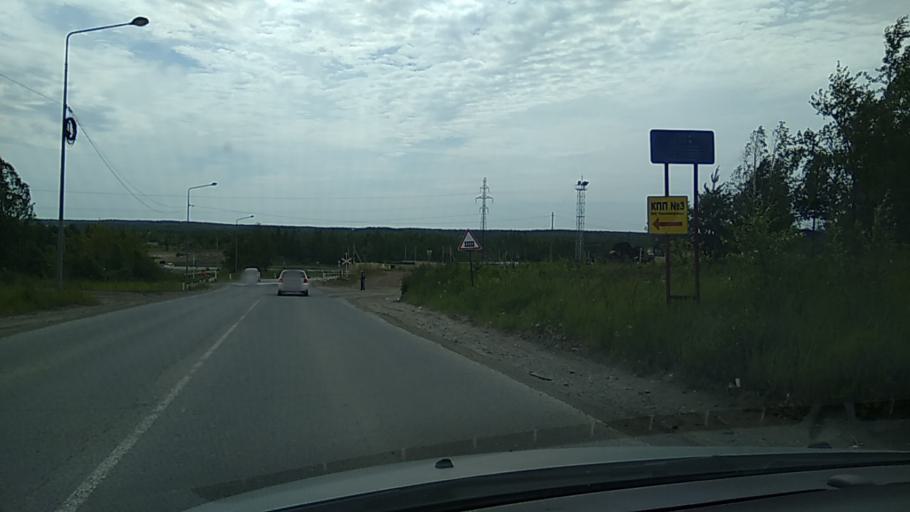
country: RU
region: Sverdlovsk
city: Verkhnyaya Pyshma
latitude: 56.9541
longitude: 60.5863
